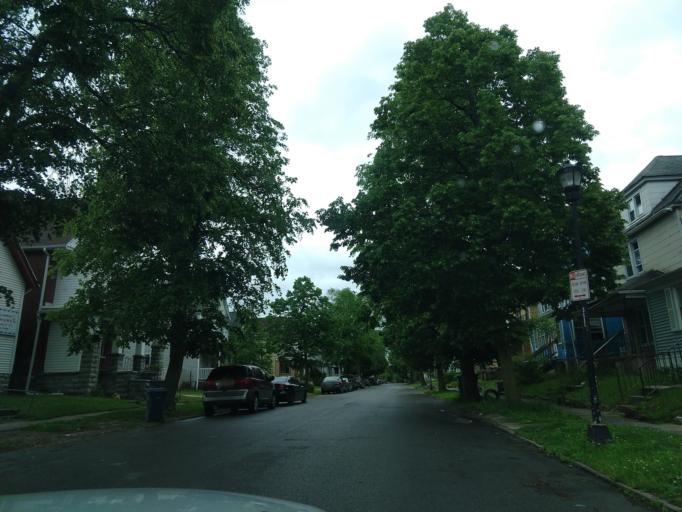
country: US
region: New York
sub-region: Erie County
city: Buffalo
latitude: 42.9168
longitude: -78.8901
